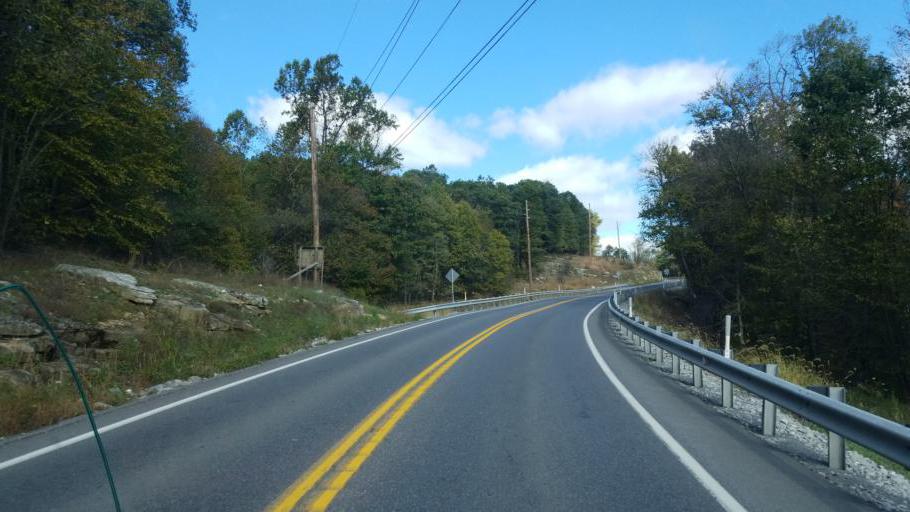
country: US
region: Pennsylvania
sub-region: Fulton County
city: McConnellsburg
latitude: 39.8720
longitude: -77.9654
